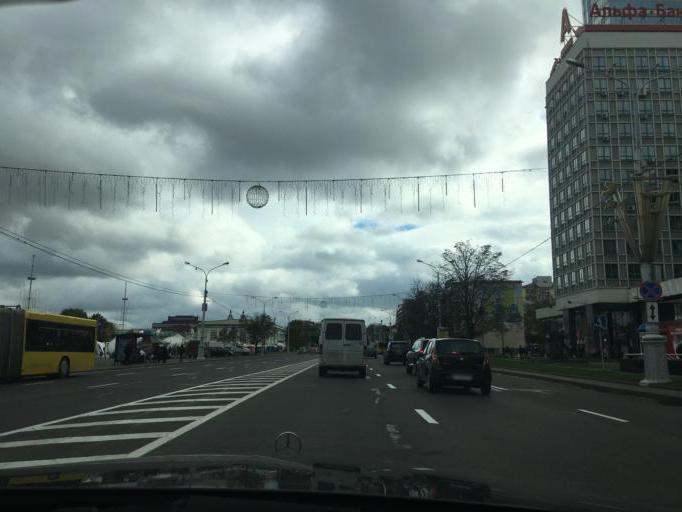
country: BY
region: Minsk
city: Minsk
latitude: 53.9092
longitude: 27.5496
